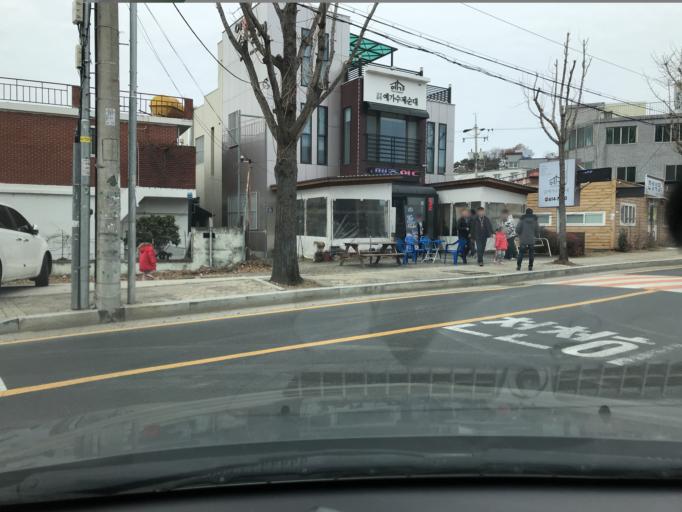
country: KR
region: Daegu
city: Hwawon
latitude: 35.6984
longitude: 128.4505
